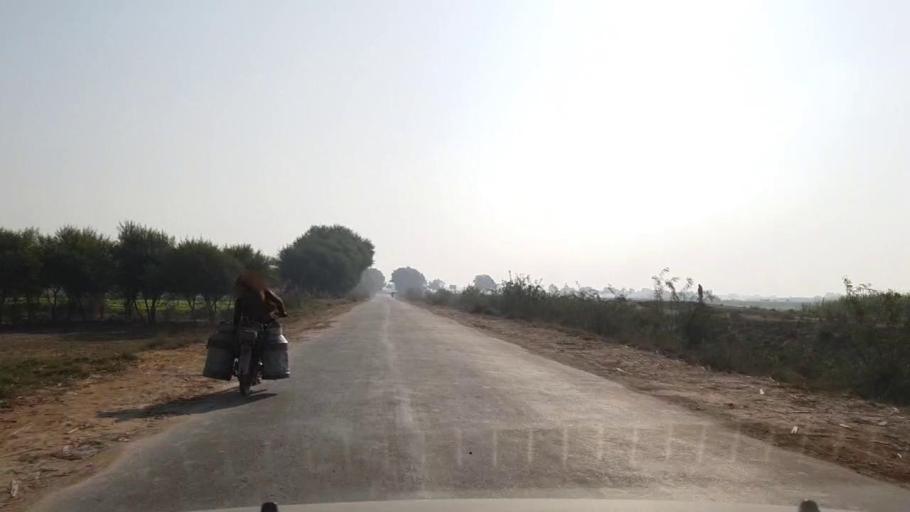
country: PK
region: Sindh
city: Matiari
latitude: 25.5864
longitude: 68.4844
